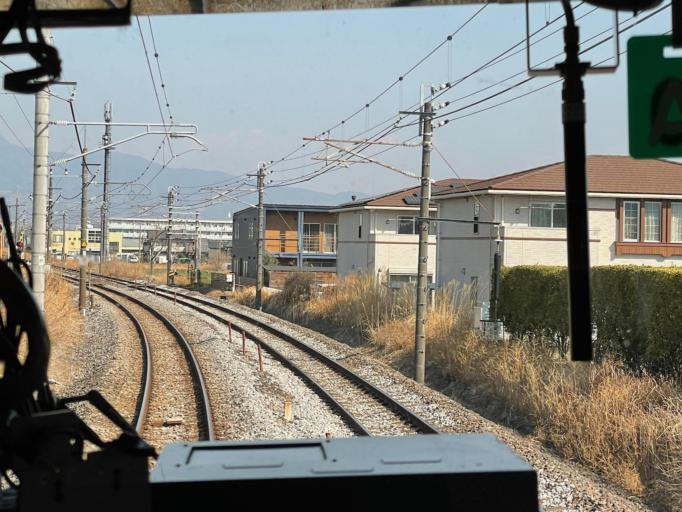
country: JP
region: Gunma
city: Shibukawa
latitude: 36.4546
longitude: 139.0208
